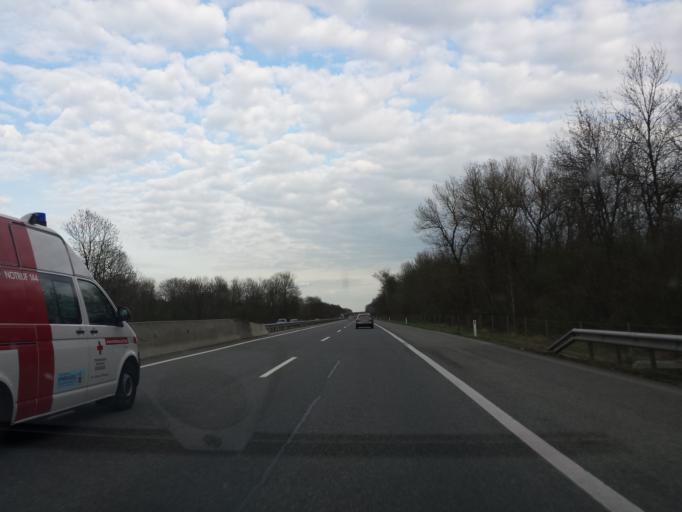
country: AT
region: Lower Austria
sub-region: Politischer Bezirk Korneuburg
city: Stetteldorf am Wagram
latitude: 48.3655
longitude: 15.9570
